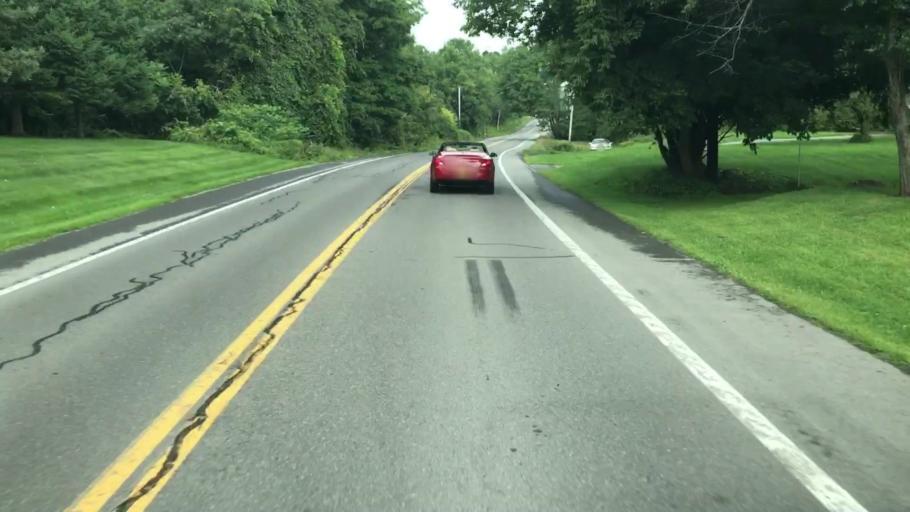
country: US
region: New York
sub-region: Onondaga County
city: Camillus
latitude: 43.0569
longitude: -76.3170
